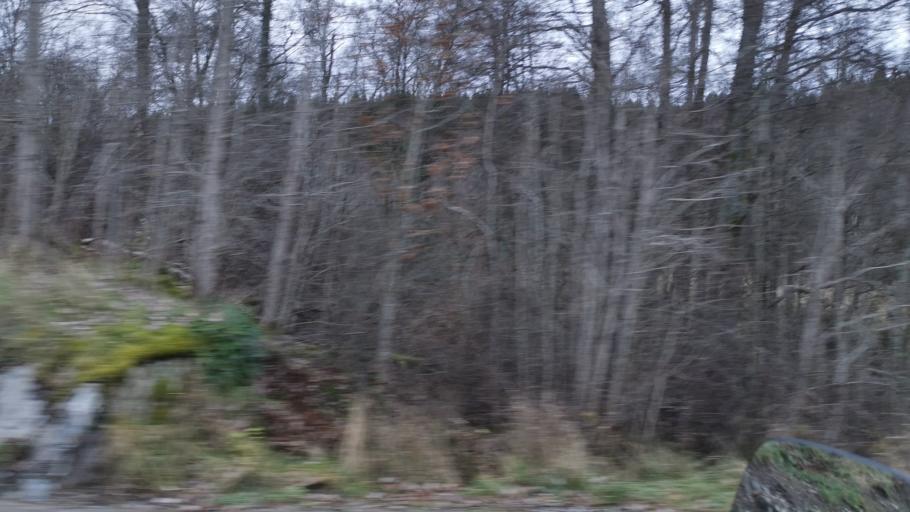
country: SE
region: Vaestra Goetaland
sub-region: Orust
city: Henan
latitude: 58.2506
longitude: 11.7210
